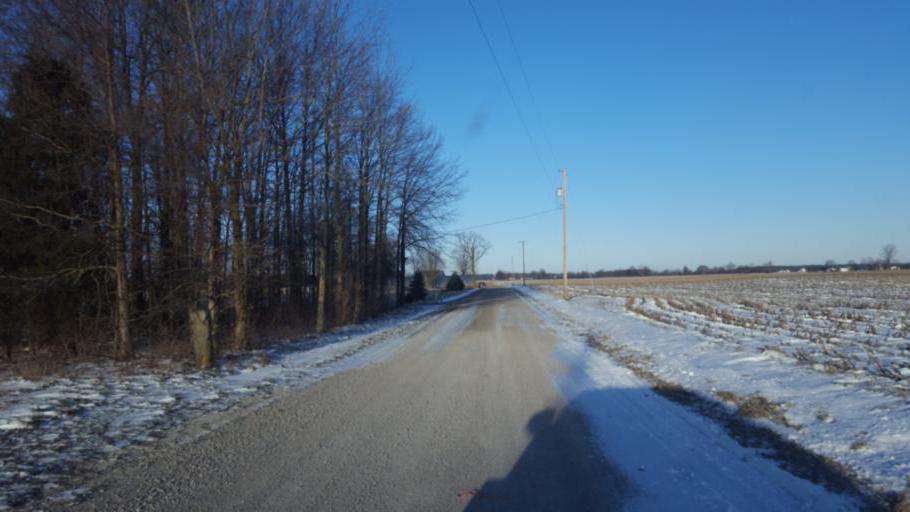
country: US
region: Ohio
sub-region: Morrow County
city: Cardington
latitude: 40.5357
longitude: -82.9241
